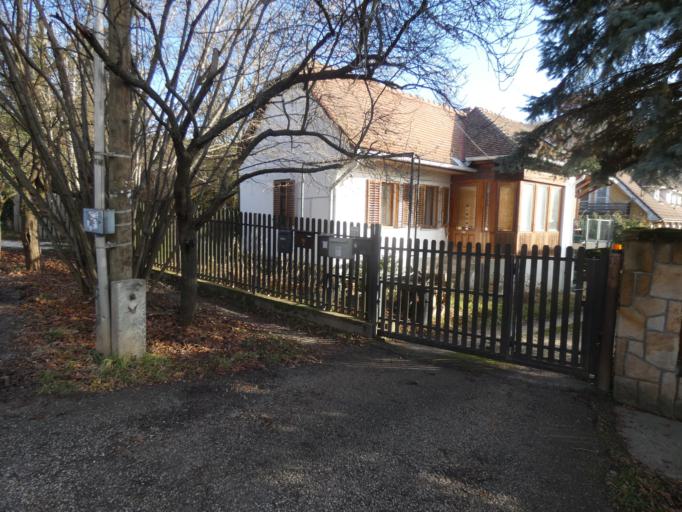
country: HU
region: Pest
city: Budakeszi
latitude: 47.5167
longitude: 18.9408
